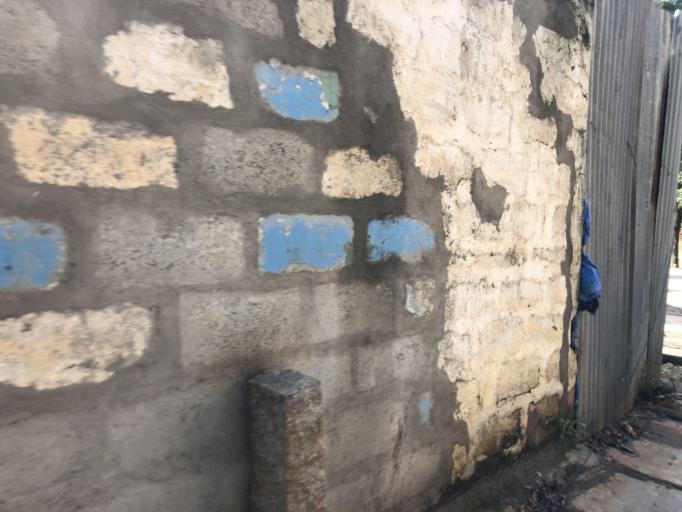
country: IN
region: Karnataka
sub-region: Bangalore Urban
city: Bangalore
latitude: 12.9216
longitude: 77.5284
